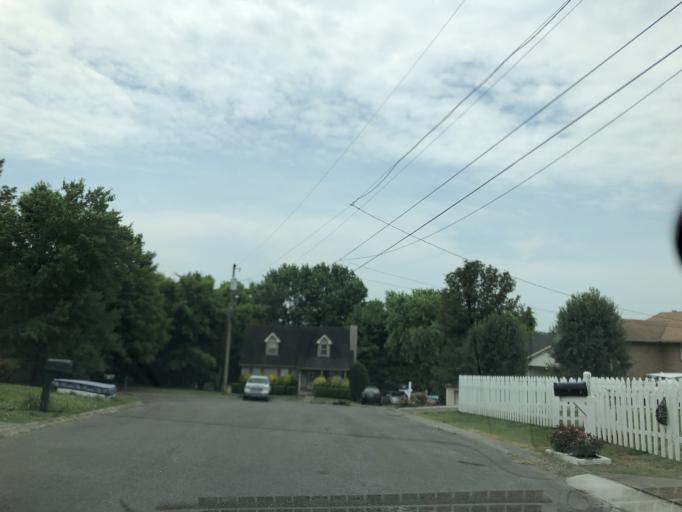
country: US
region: Tennessee
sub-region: Rutherford County
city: La Vergne
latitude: 36.0663
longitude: -86.6743
